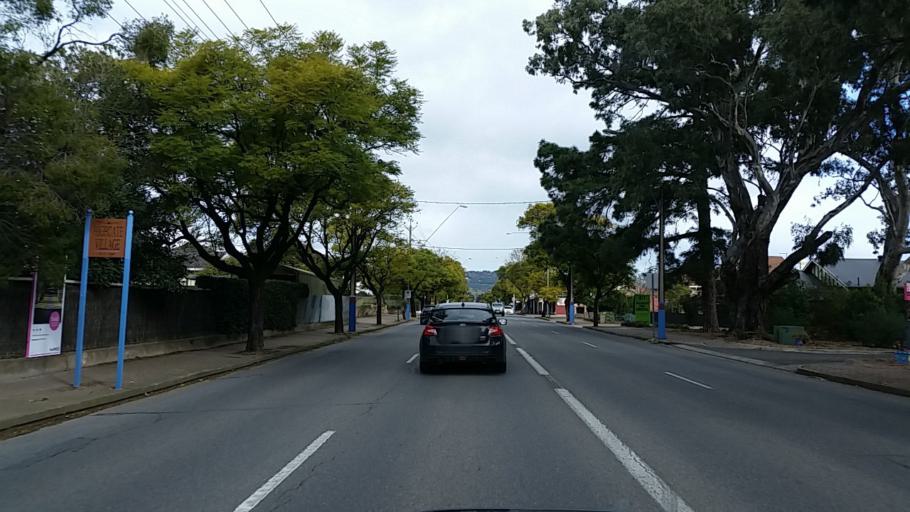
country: AU
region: South Australia
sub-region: Unley
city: Fullarton
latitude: -34.9579
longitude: 138.6260
